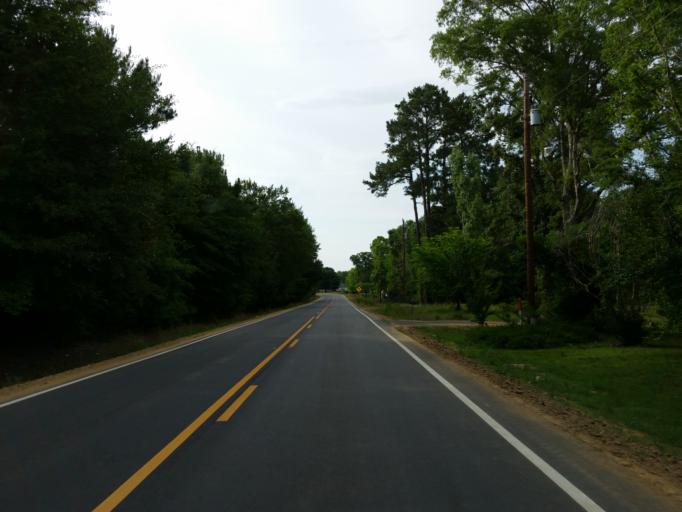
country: US
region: Georgia
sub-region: Turner County
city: Ashburn
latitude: 31.7635
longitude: -83.6849
